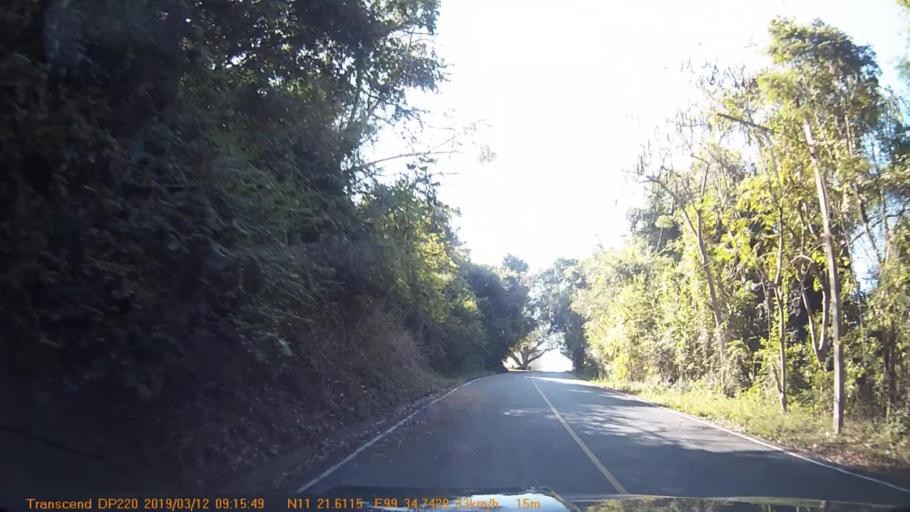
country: TH
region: Prachuap Khiri Khan
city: Thap Sakae
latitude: 11.3601
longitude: 99.5791
